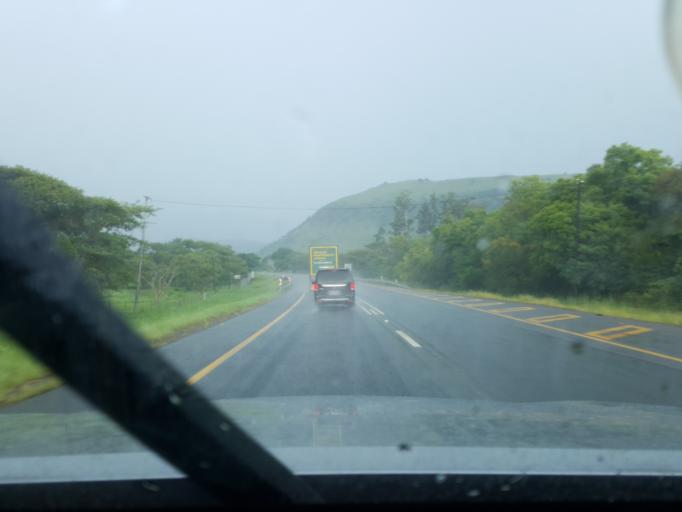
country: ZA
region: Mpumalanga
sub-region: Nkangala District Municipality
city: Belfast
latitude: -25.6075
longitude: 30.4342
